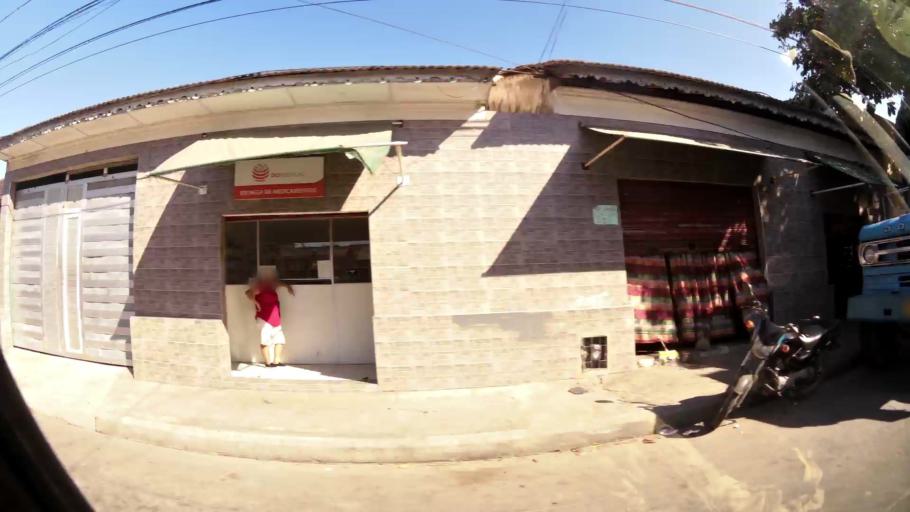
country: CO
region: Atlantico
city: Barranquilla
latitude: 10.9735
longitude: -74.7813
